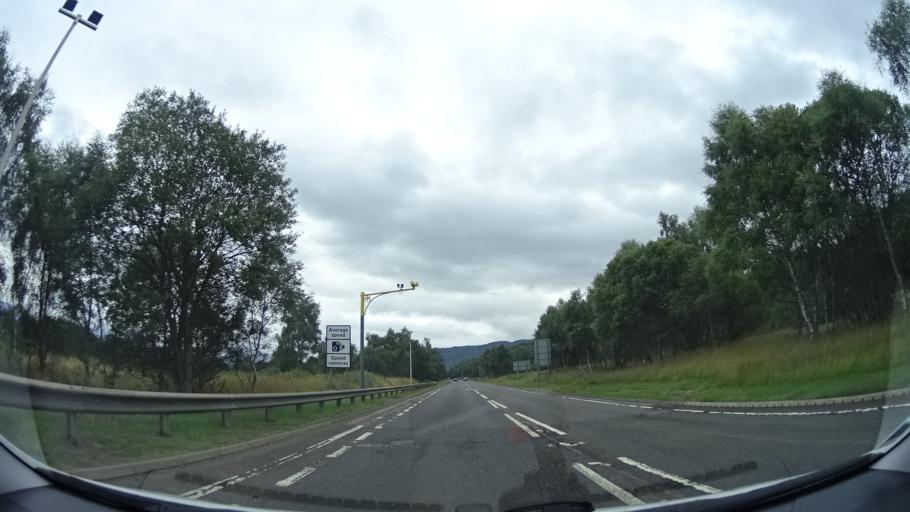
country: GB
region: Scotland
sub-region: Highland
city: Aviemore
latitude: 57.2130
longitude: -3.8252
